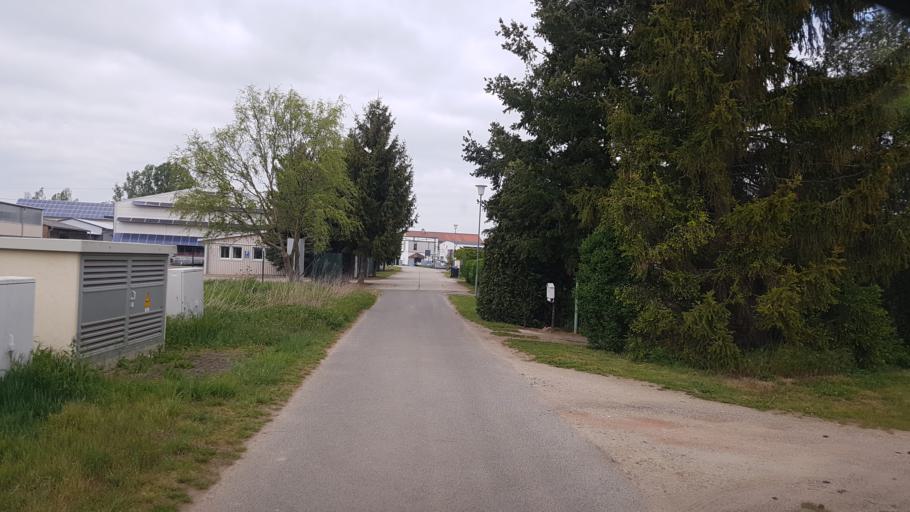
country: DE
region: Brandenburg
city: Sonnewalde
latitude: 51.6893
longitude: 13.6336
